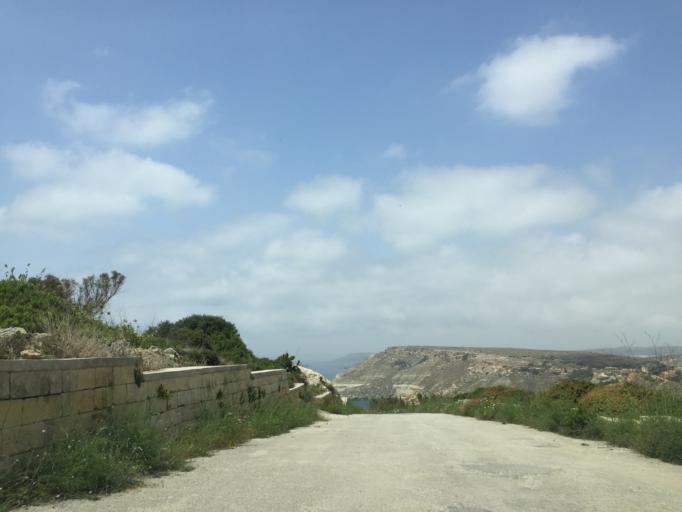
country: MT
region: L-Imgarr
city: Imgarr
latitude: 35.9015
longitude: 14.3367
